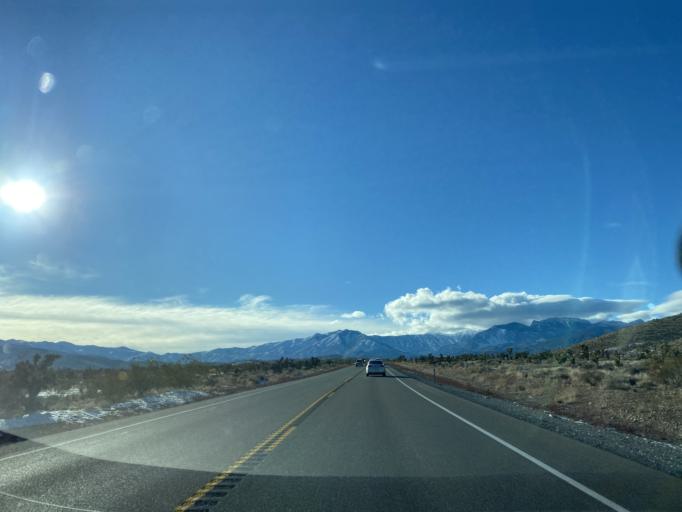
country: US
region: Nevada
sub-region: Clark County
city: Summerlin South
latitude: 36.2816
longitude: -115.4435
